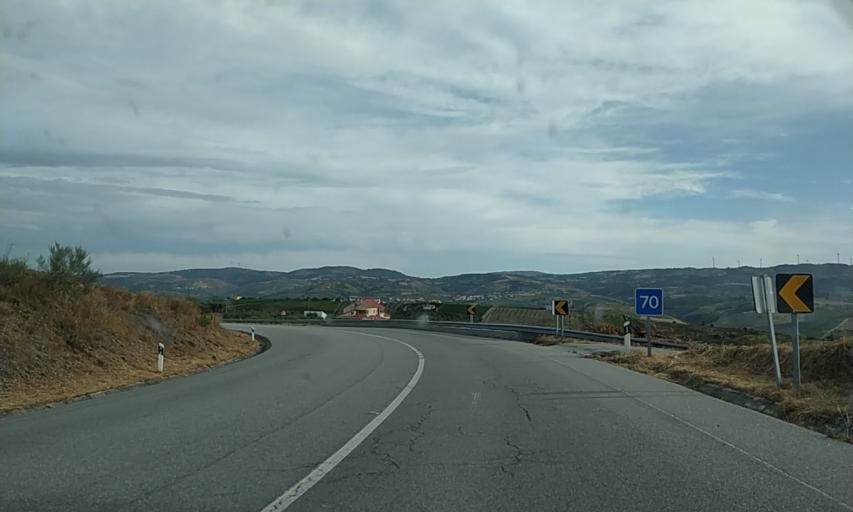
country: PT
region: Viseu
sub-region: Sao Joao da Pesqueira
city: Sao Joao da Pesqueira
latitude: 41.1084
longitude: -7.3888
